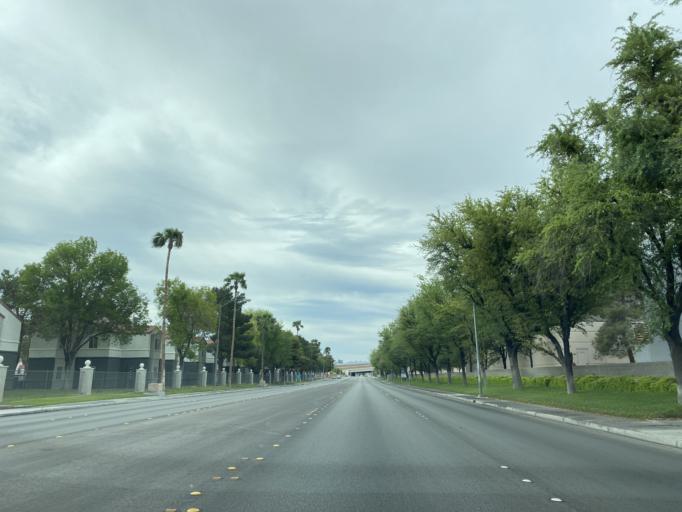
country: US
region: Nevada
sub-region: Clark County
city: Paradise
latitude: 36.0638
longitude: -115.1412
